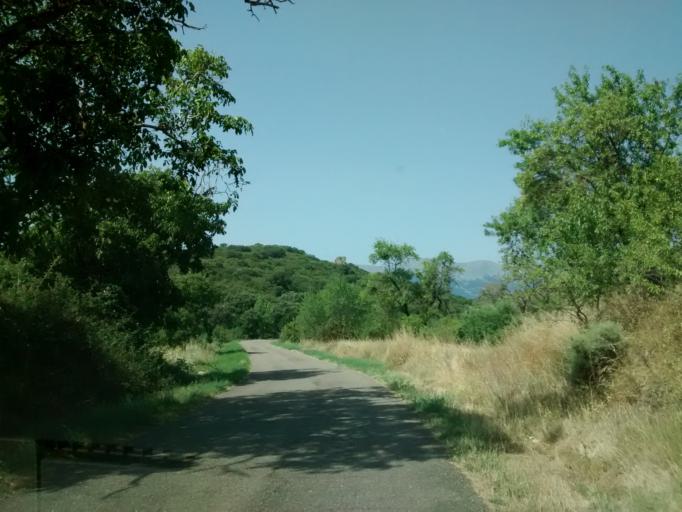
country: ES
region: Aragon
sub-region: Provincia de Zaragoza
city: Vera de Moncayo
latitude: 41.8123
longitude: -1.7033
